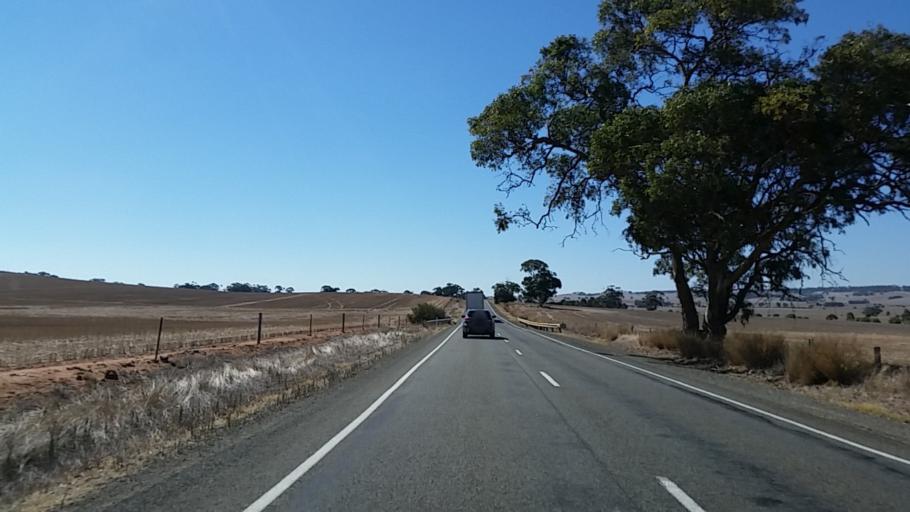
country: AU
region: South Australia
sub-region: Clare and Gilbert Valleys
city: Clare
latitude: -34.0191
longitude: 138.8085
